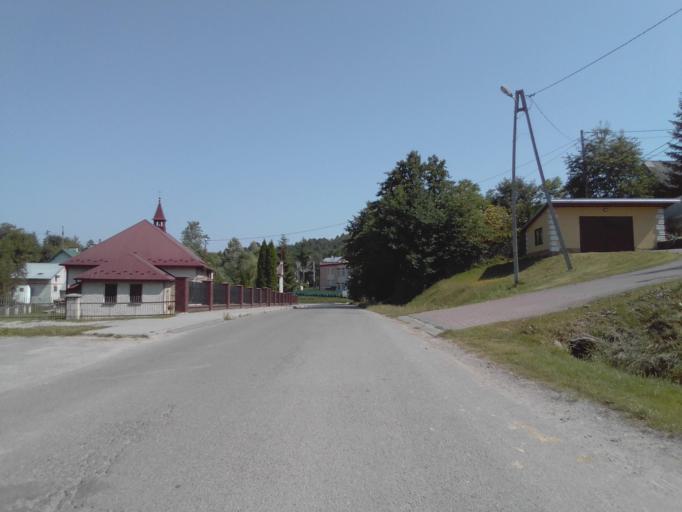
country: PL
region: Subcarpathian Voivodeship
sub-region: Powiat ropczycko-sedziszowski
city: Zagorzyce
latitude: 50.0165
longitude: 21.6365
